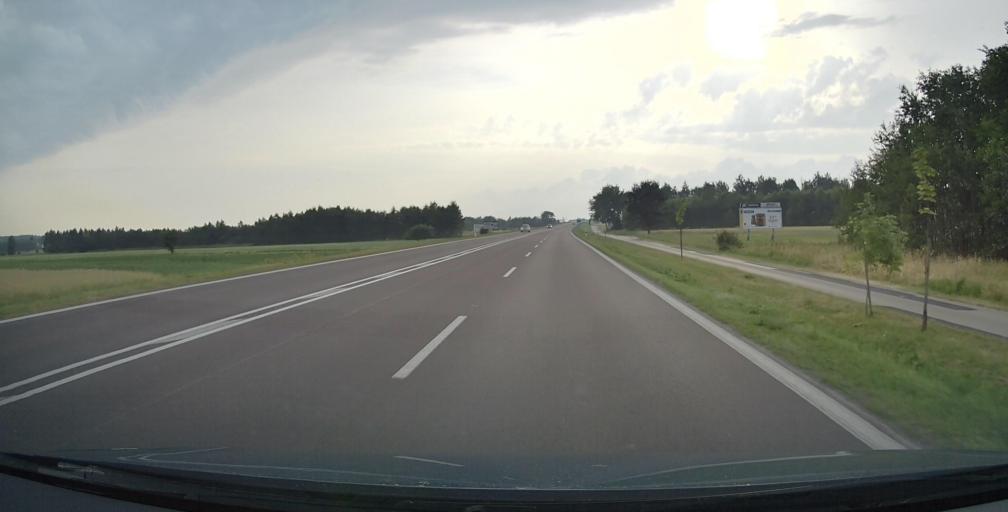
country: PL
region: Masovian Voivodeship
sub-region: Siedlce
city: Siedlce
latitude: 52.1317
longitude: 22.3180
